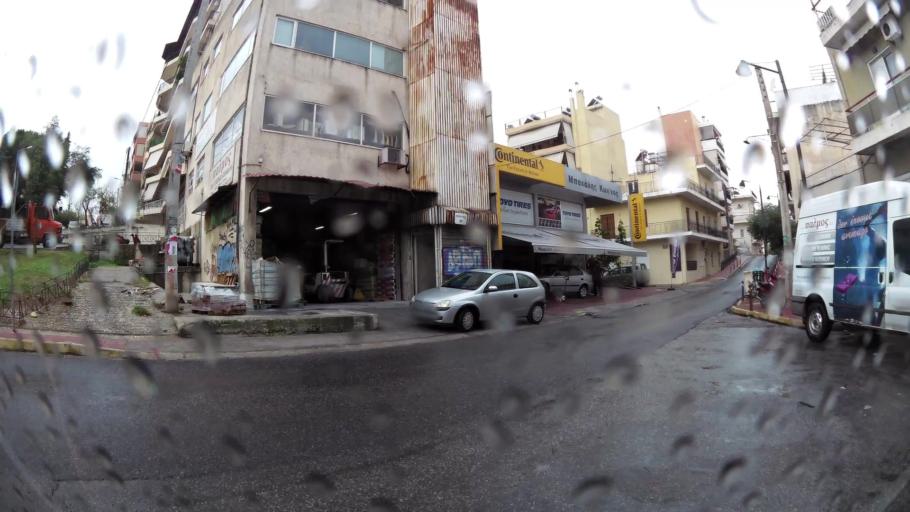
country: GR
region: Attica
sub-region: Nomarchia Athinas
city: Ymittos
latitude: 37.9538
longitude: 23.7559
